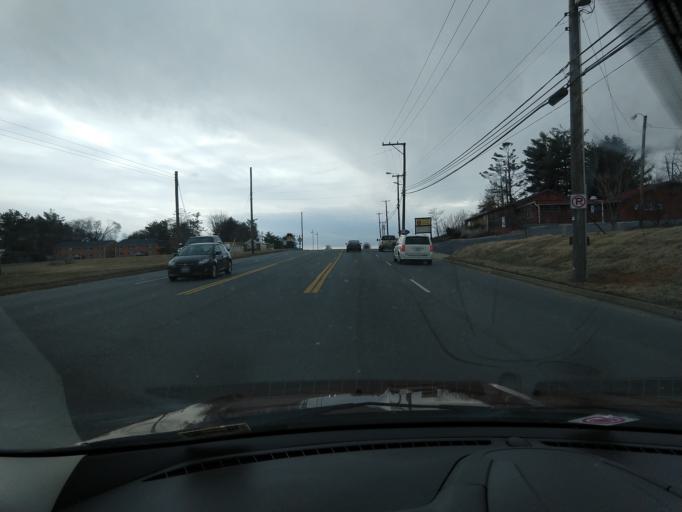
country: US
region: Virginia
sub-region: City of Waynesboro
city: Waynesboro
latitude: 38.0780
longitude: -78.9182
